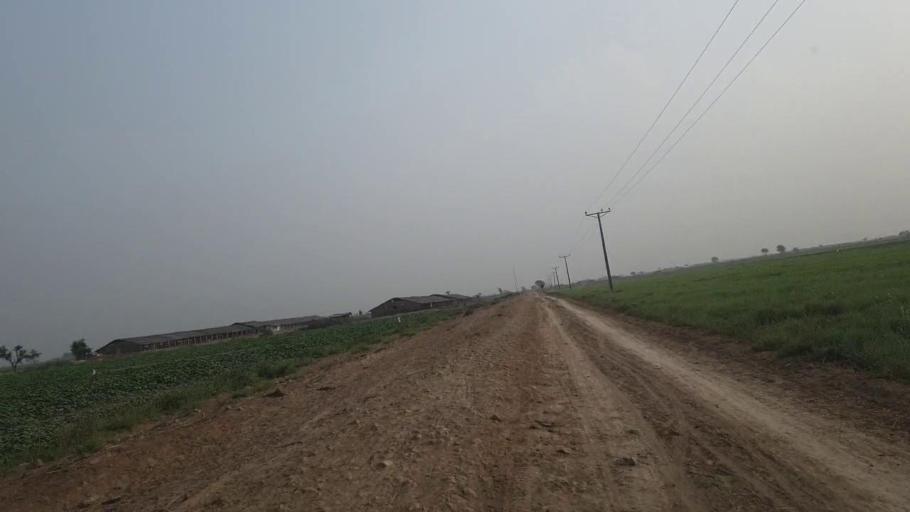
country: PK
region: Sindh
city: Mirpur Batoro
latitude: 24.5529
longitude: 68.4206
